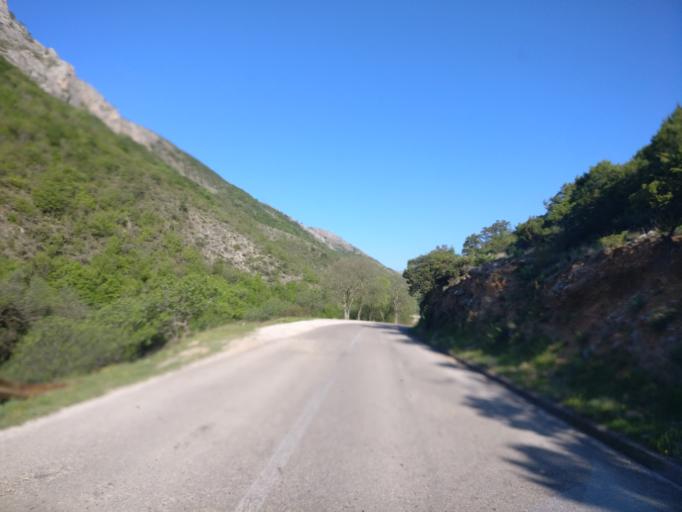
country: BA
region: Federation of Bosnia and Herzegovina
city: Stolac
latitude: 43.0814
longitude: 18.0116
